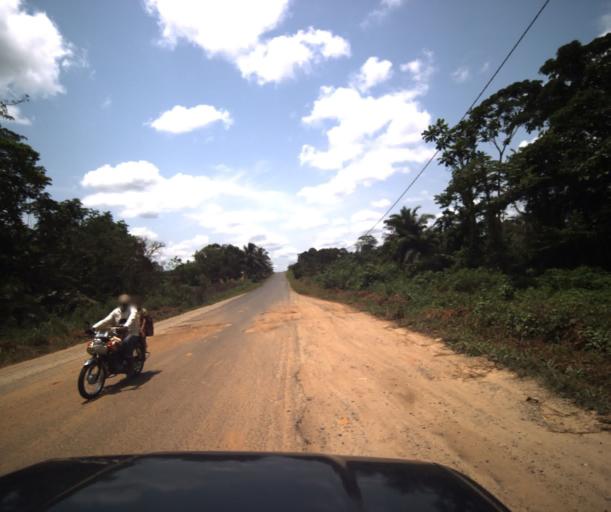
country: CM
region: Centre
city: Eseka
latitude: 3.7150
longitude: 10.7977
